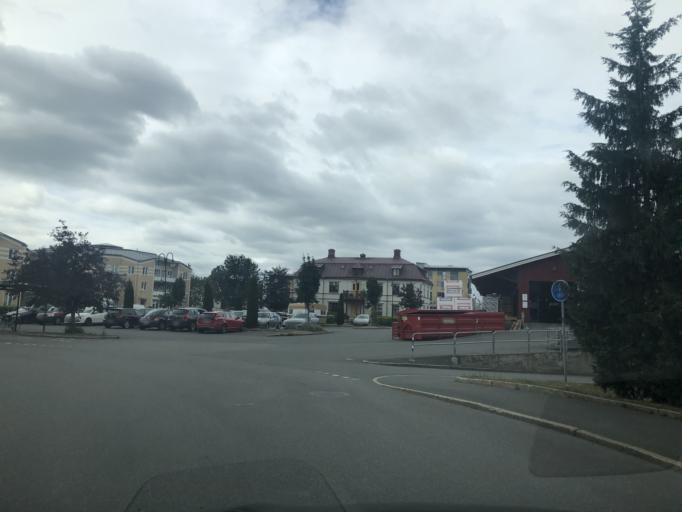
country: SE
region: Joenkoeping
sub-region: Vaggeryds Kommun
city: Vaggeryd
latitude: 57.4983
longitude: 14.1463
